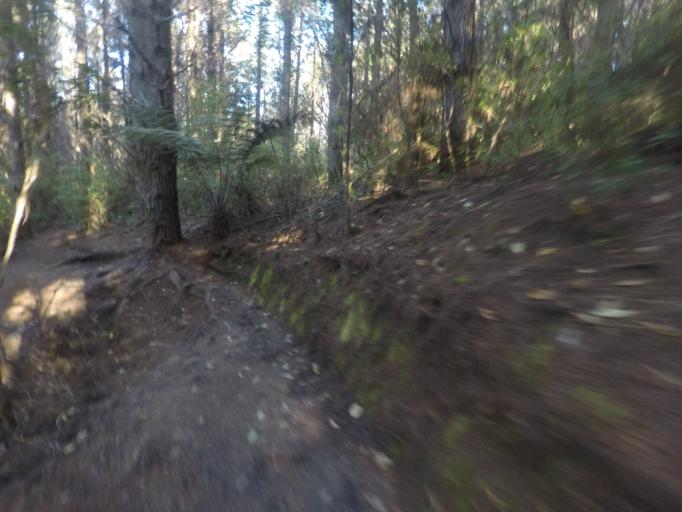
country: NZ
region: Auckland
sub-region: Auckland
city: Muriwai Beach
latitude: -36.7488
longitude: 174.5683
